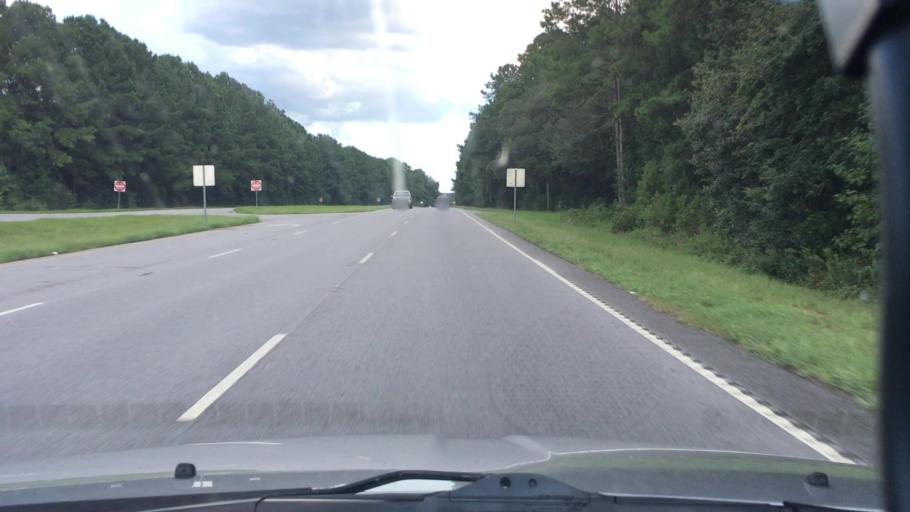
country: US
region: South Carolina
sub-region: Hampton County
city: Yemassee
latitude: 32.6295
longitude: -80.8331
